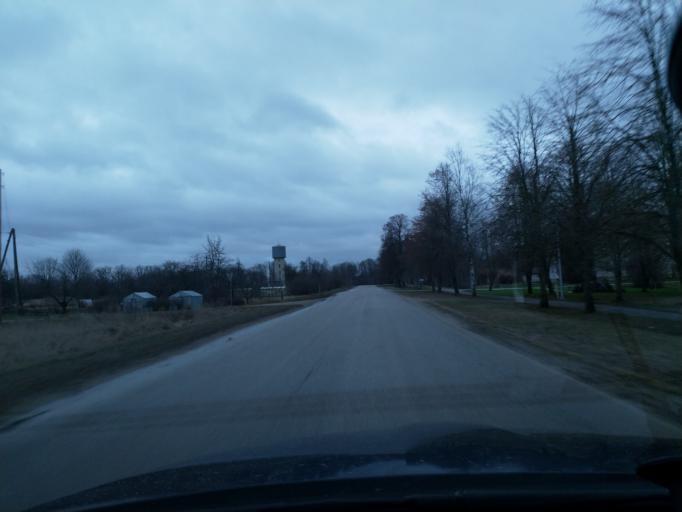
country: LV
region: Broceni
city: Broceni
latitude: 56.8574
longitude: 22.3834
